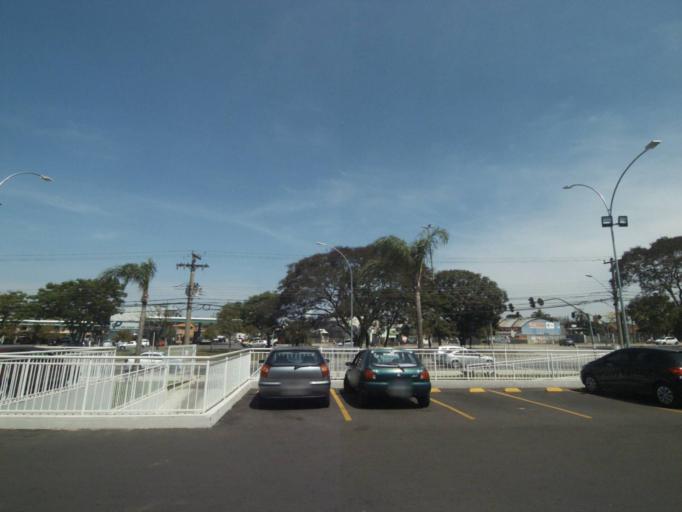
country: BR
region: Parana
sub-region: Curitiba
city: Curitiba
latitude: -25.4716
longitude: -49.2628
